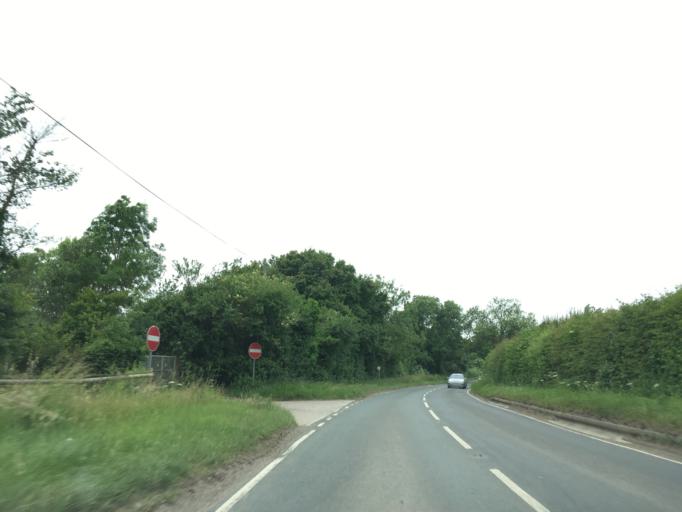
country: GB
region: England
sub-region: Gloucestershire
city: Stonehouse
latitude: 51.7619
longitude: -2.3445
